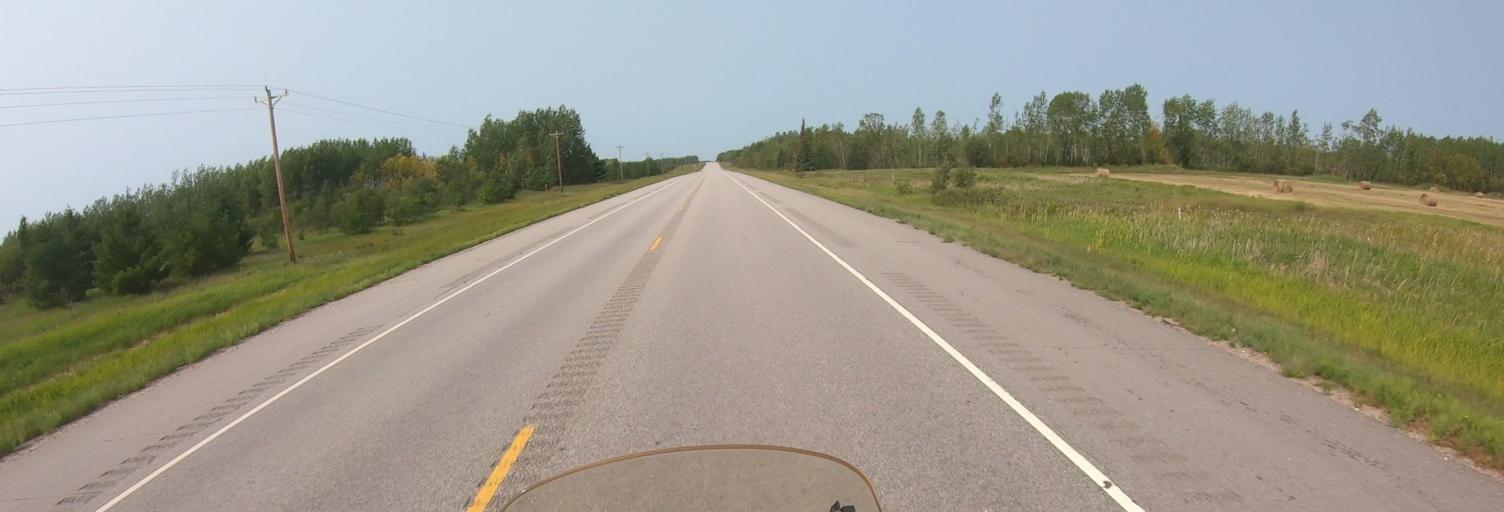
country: CA
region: Ontario
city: Fort Frances
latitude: 48.4101
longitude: -93.1456
